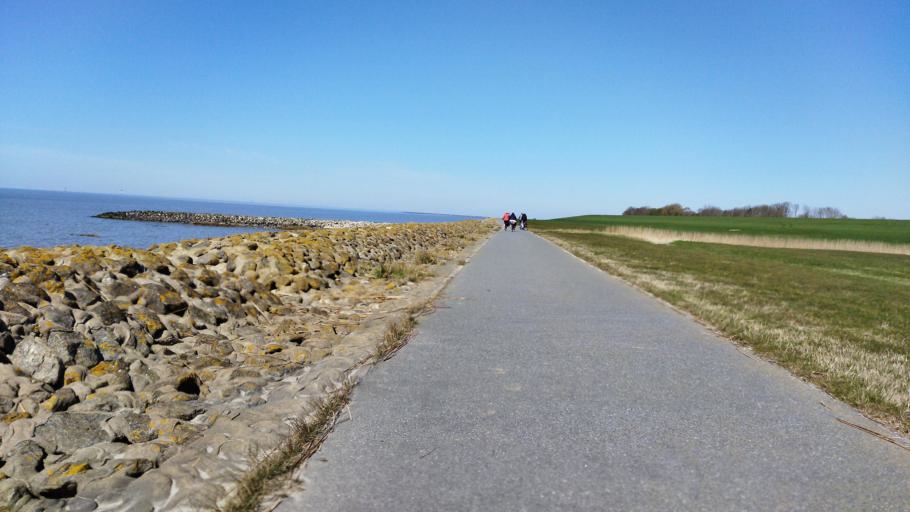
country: DE
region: Lower Saxony
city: Wremen
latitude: 53.6227
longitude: 8.5096
